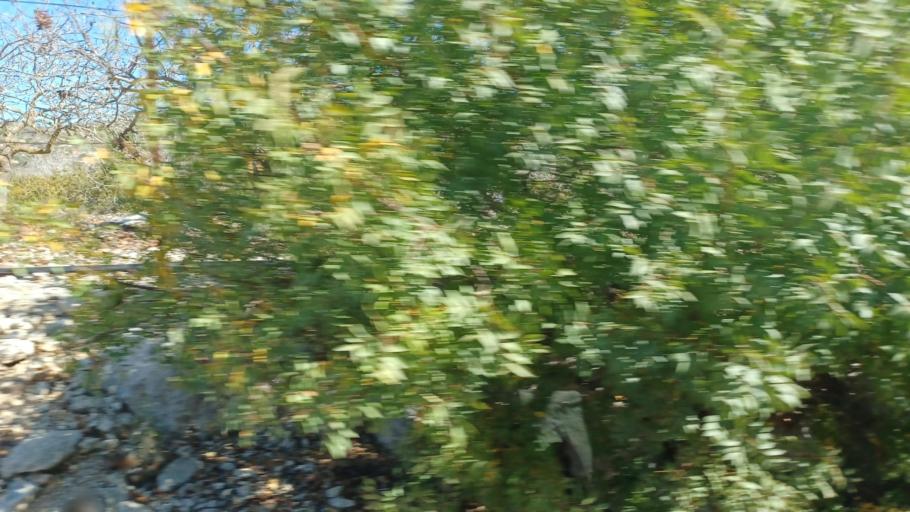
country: CY
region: Pafos
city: Mesogi
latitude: 34.8136
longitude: 32.4770
